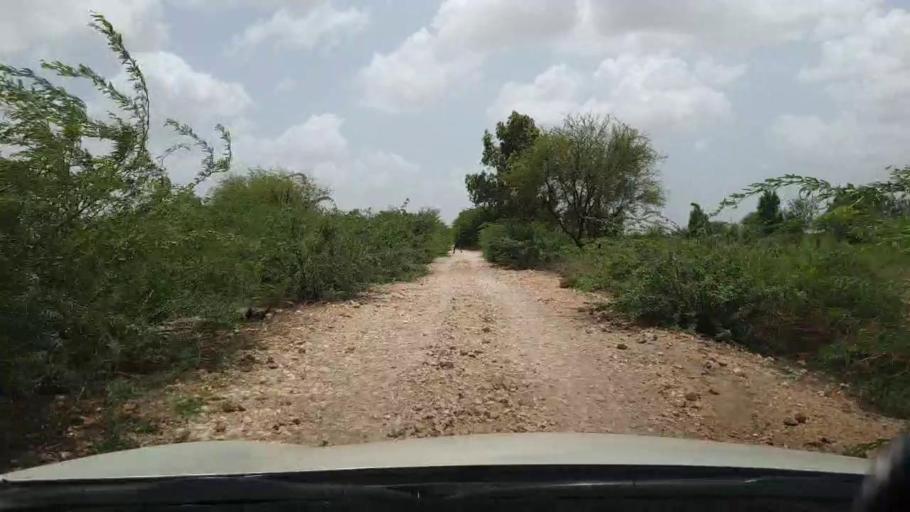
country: PK
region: Sindh
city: Kadhan
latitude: 24.3756
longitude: 68.9287
